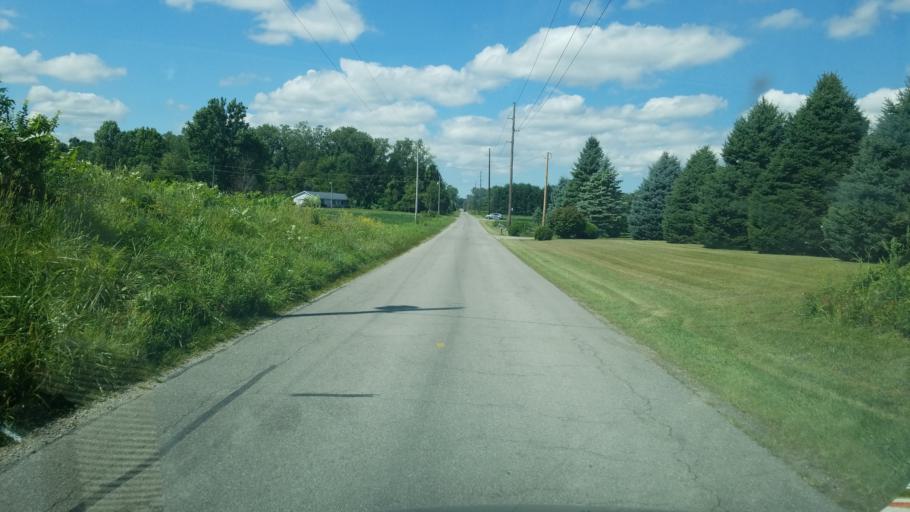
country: US
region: Ohio
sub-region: Henry County
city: Liberty Center
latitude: 41.4512
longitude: -83.8995
